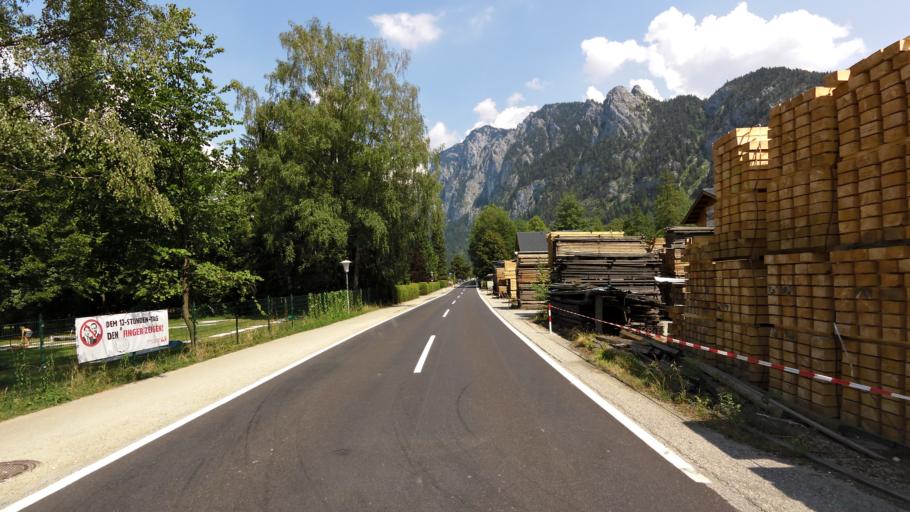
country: AT
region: Upper Austria
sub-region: Politischer Bezirk Vocklabruck
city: Steinbach am Attersee
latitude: 47.7976
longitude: 13.5321
